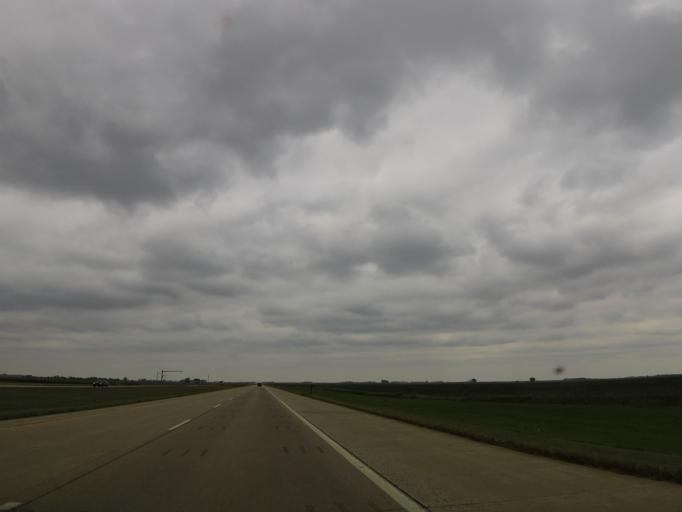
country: US
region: South Dakota
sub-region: Roberts County
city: Sisseton
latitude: 45.7080
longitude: -96.9591
